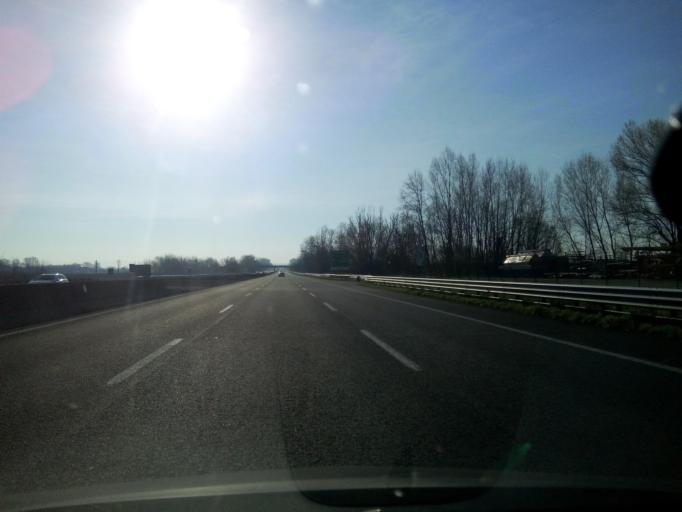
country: IT
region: Emilia-Romagna
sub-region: Provincia di Modena
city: Campogalliano
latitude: 44.6725
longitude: 10.8302
